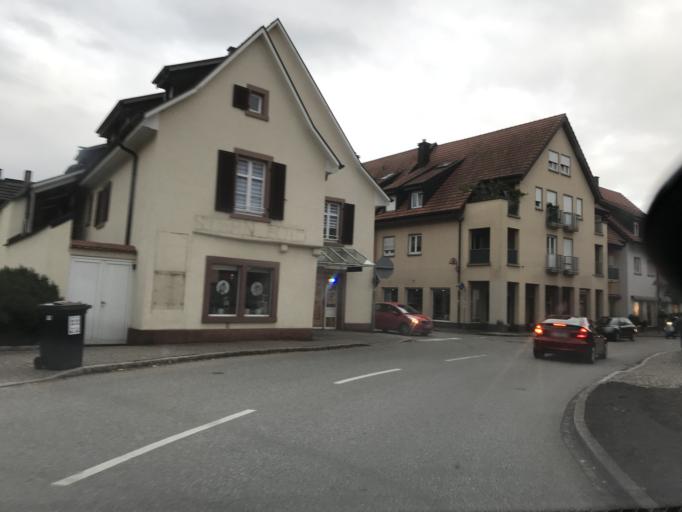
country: DE
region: Baden-Wuerttemberg
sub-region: Freiburg Region
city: Steinen
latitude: 47.6436
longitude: 7.7395
